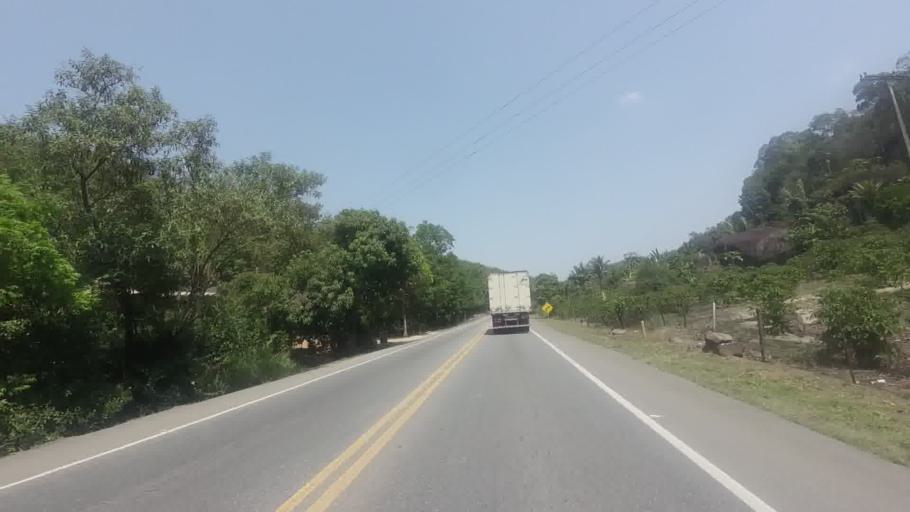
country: BR
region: Espirito Santo
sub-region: Iconha
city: Iconha
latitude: -20.8323
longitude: -40.8602
